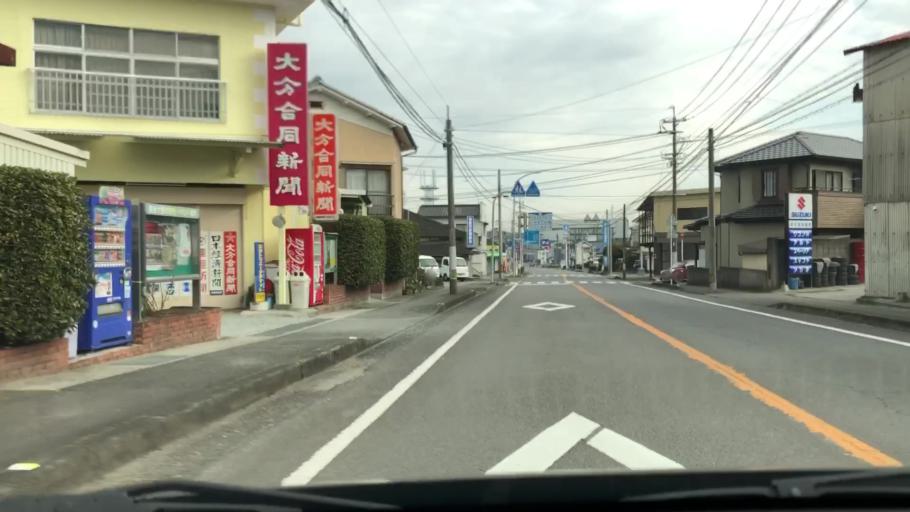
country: JP
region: Oita
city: Takedamachi
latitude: 32.9743
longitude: 131.5802
